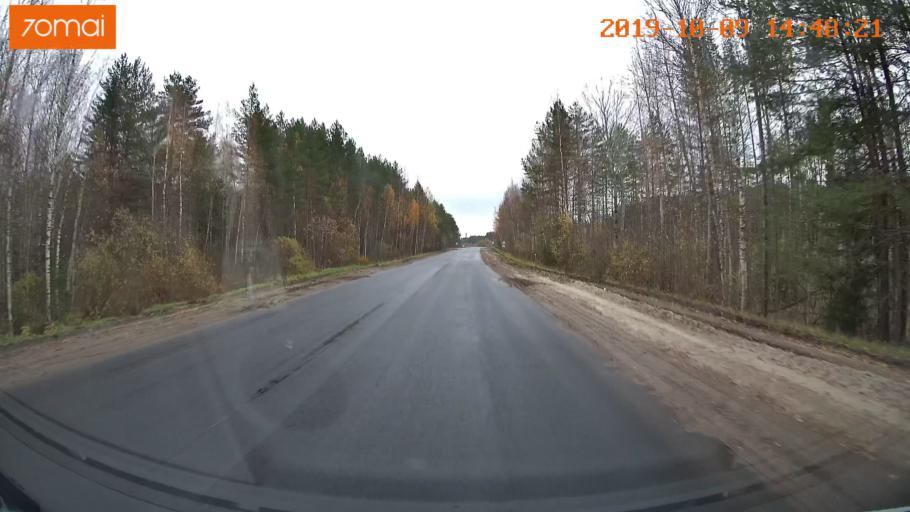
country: RU
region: Kostroma
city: Chistyye Bory
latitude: 58.4067
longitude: 41.5750
